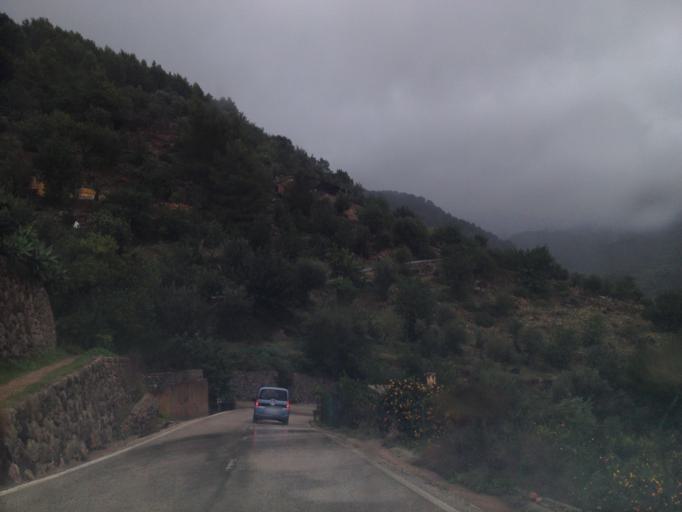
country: ES
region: Balearic Islands
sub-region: Illes Balears
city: Fornalutx
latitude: 39.7857
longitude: 2.7398
